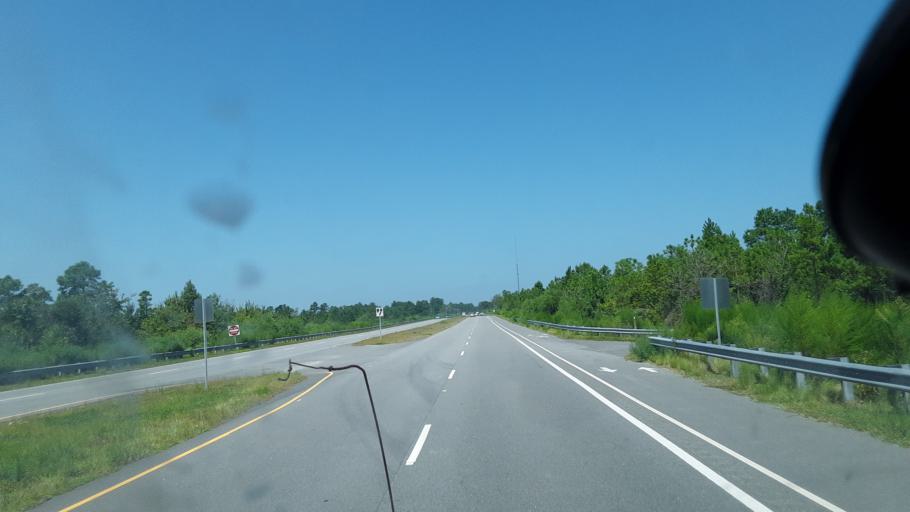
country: US
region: South Carolina
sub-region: Horry County
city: Forestbrook
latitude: 33.8092
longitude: -78.8964
